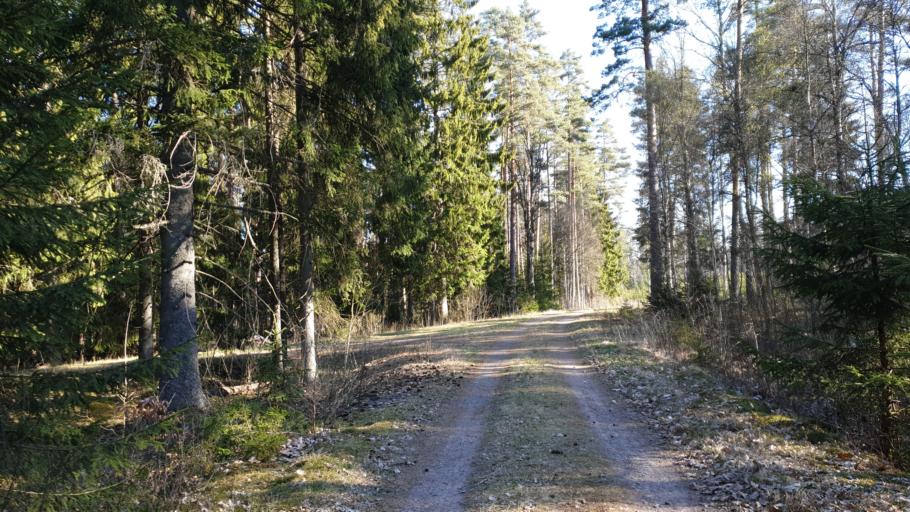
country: SE
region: Kronoberg
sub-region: Ljungby Kommun
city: Ljungby
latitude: 56.8320
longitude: 13.9025
